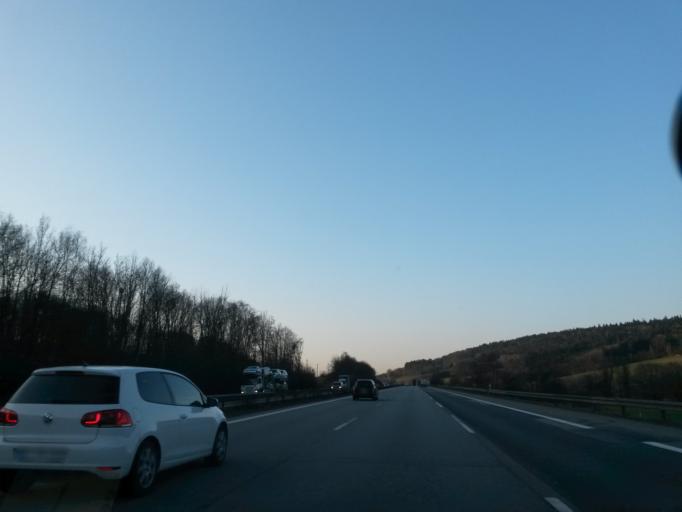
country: DE
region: Bavaria
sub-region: Regierungsbezirk Mittelfranken
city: Thalmassing
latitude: 49.0975
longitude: 11.2854
